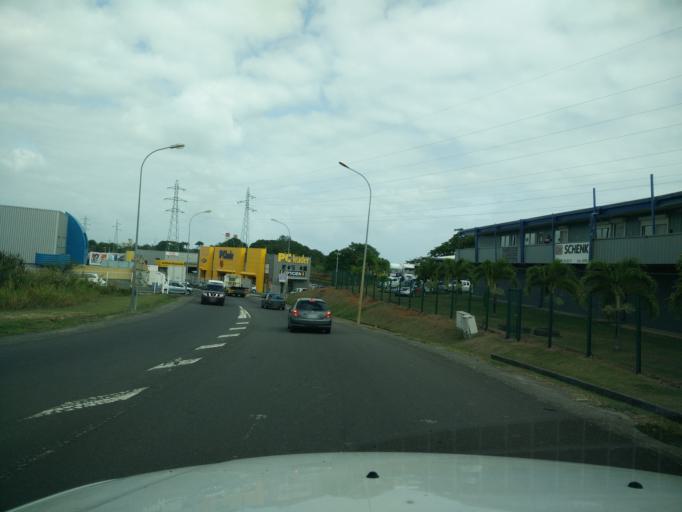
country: GP
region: Guadeloupe
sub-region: Guadeloupe
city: Pointe-a-Pitre
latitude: 16.2378
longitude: -61.5694
